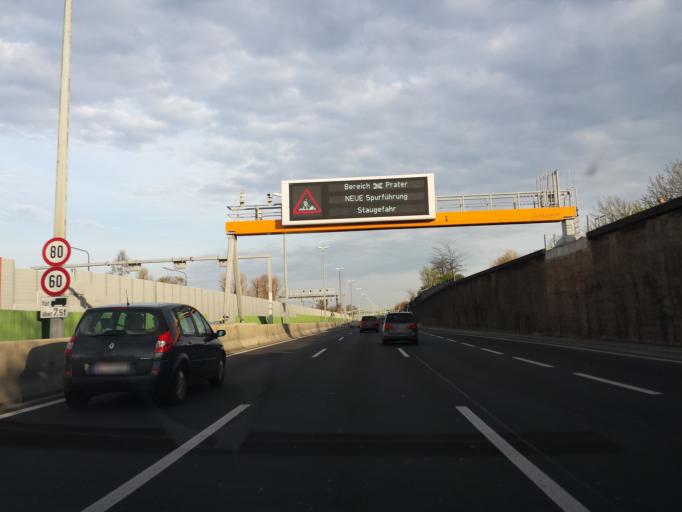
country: AT
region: Vienna
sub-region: Wien Stadt
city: Vienna
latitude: 48.2184
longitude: 16.4298
